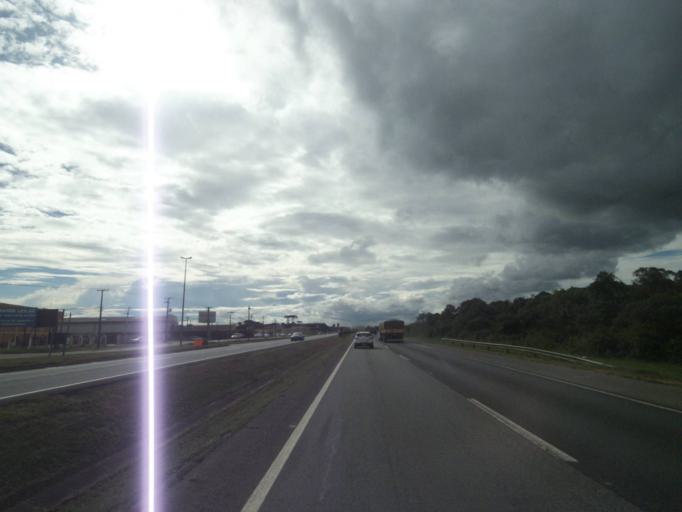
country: BR
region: Parana
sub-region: Piraquara
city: Piraquara
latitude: -25.5320
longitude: -49.0819
